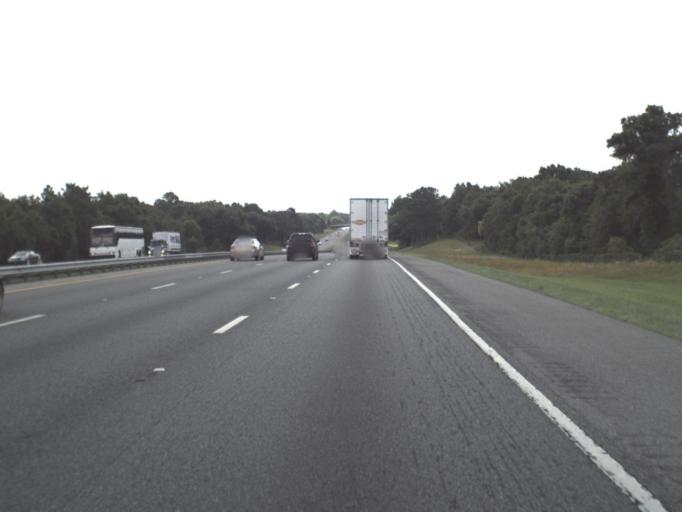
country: US
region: Florida
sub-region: Columbia County
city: Five Points
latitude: 30.2283
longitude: -82.7228
